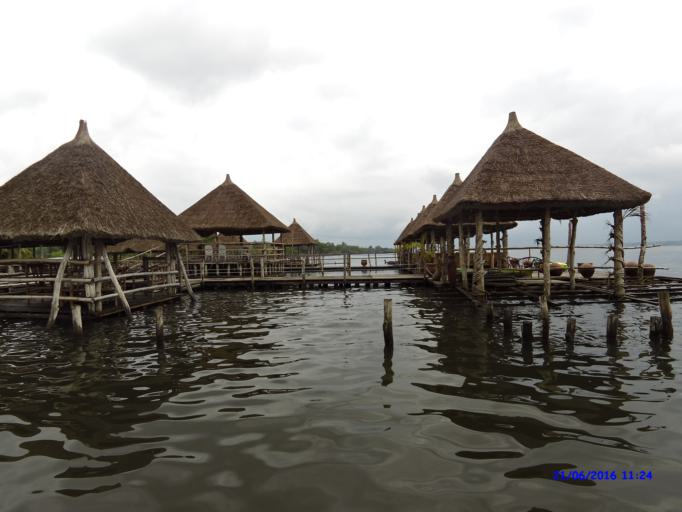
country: BJ
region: Mono
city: Come
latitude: 6.5325
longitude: 1.9711
